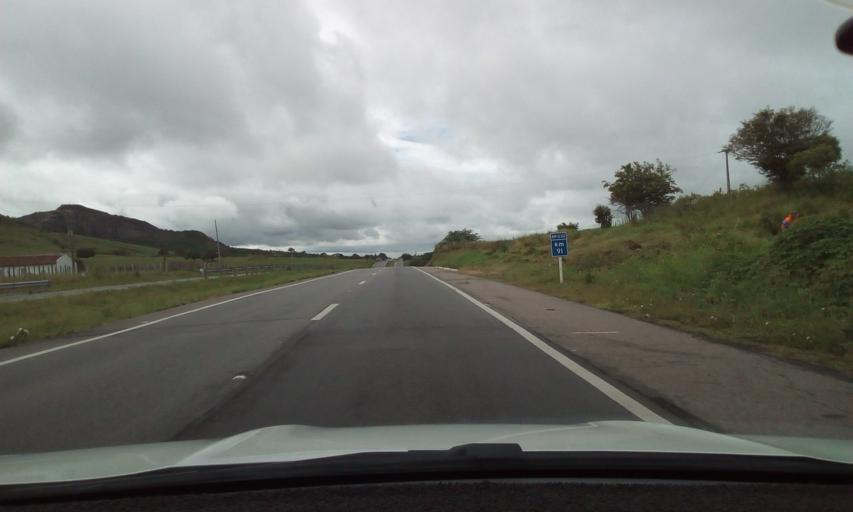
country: BR
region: Paraiba
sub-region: Gurinhem
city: Gurinhem
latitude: -7.1767
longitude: -35.4129
